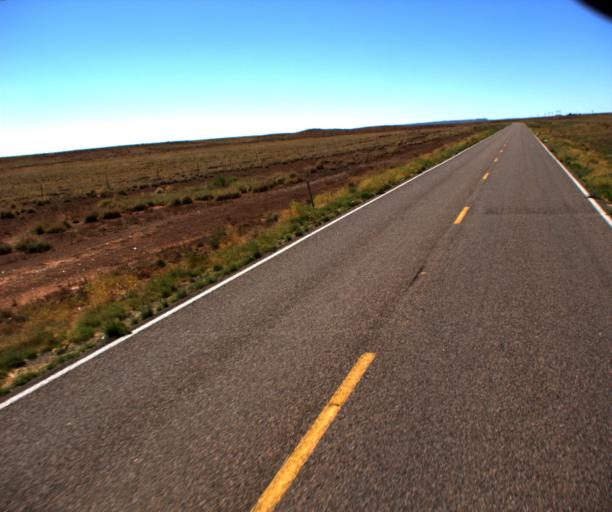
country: US
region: Arizona
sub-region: Coconino County
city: LeChee
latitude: 35.1667
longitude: -110.9144
